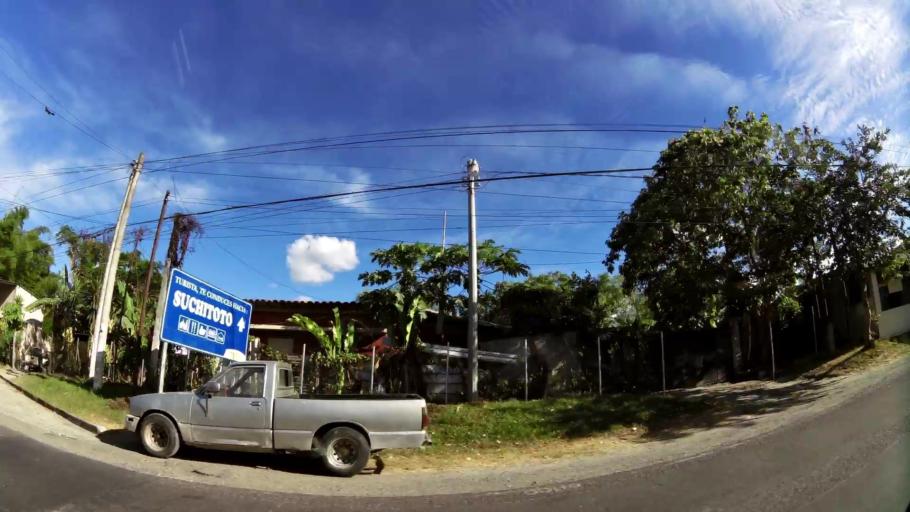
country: SV
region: Cuscatlan
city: Tecoluca
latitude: 13.7643
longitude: -89.0467
